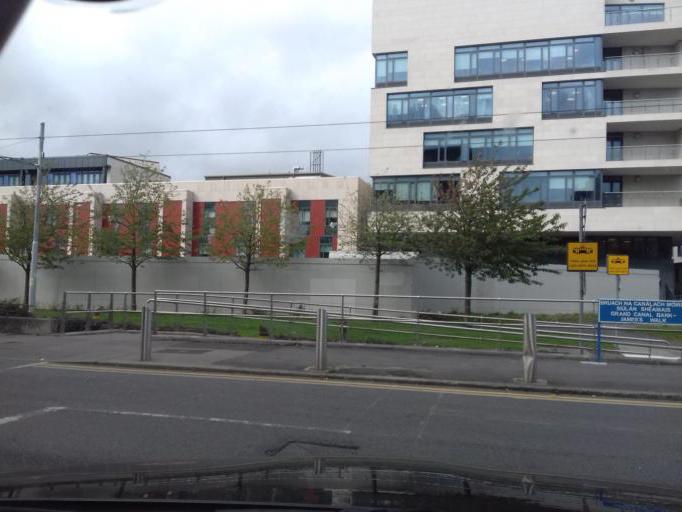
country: IE
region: Leinster
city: Rialto
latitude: 53.3382
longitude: -6.2929
